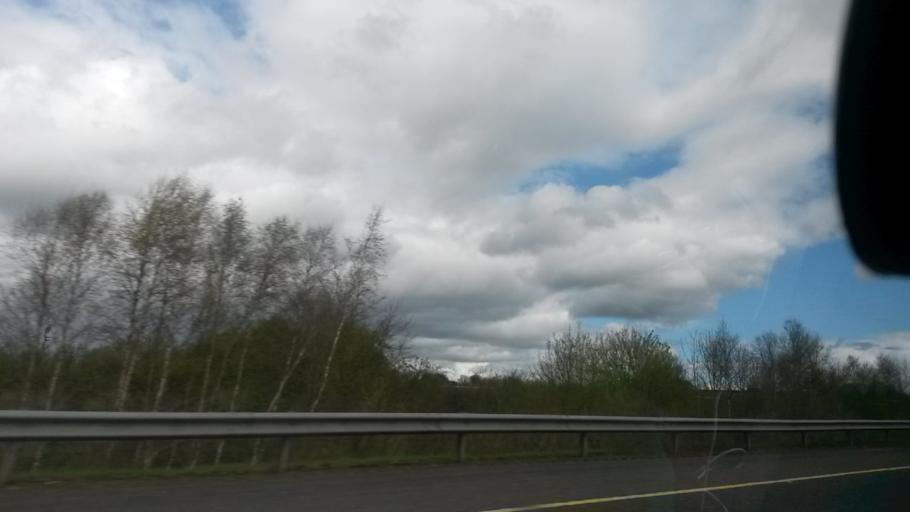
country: IE
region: Leinster
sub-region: Kildare
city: Cherryville
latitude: 53.1541
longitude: -6.9582
